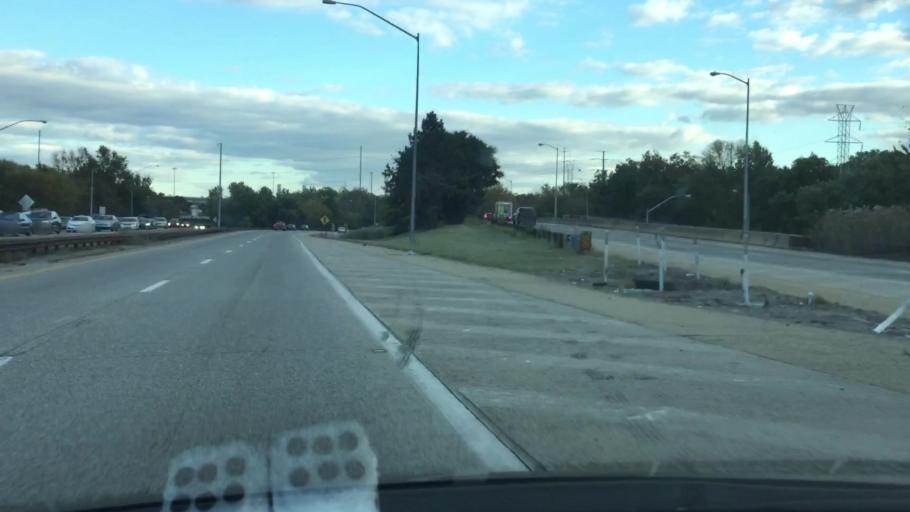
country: US
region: Pennsylvania
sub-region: Delaware County
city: Woodlyn
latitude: 39.8718
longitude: -75.3487
